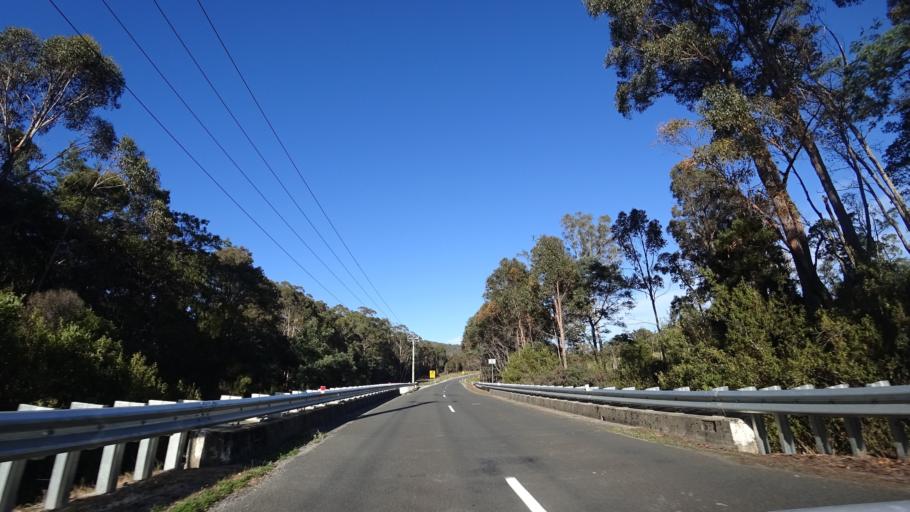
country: AU
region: Tasmania
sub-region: Break O'Day
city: St Helens
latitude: -41.2829
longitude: 148.1325
